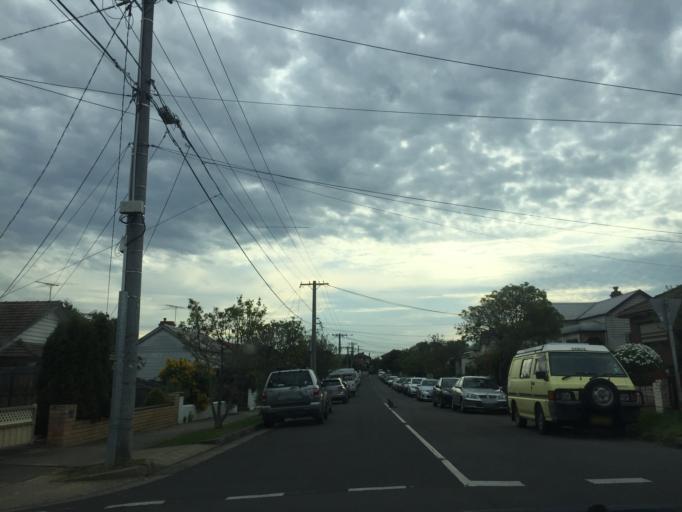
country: AU
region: Victoria
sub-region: Darebin
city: Thornbury
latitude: -37.7524
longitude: 145.0088
